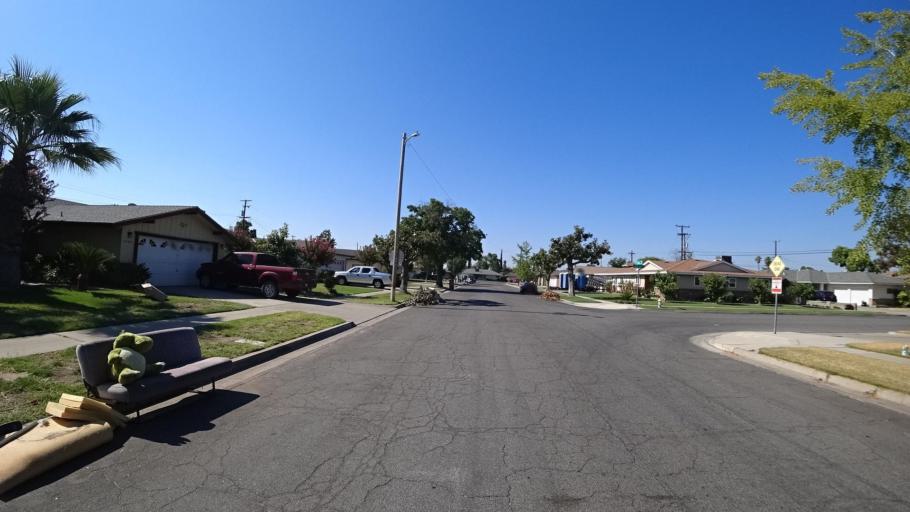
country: US
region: California
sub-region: Fresno County
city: Fresno
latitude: 36.7825
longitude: -119.7508
